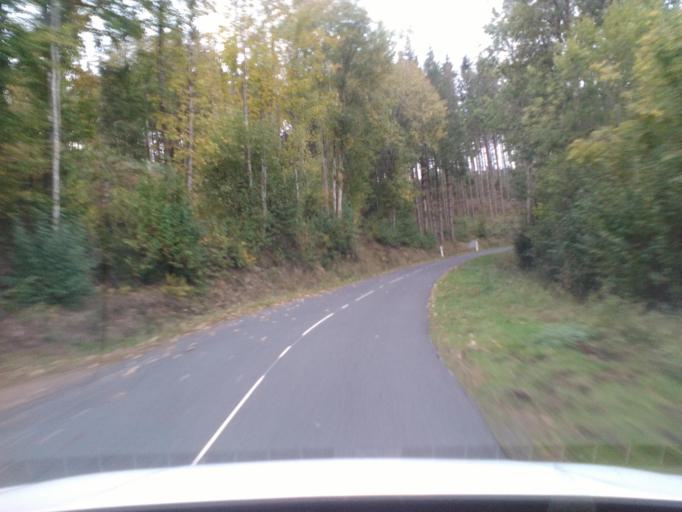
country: FR
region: Lorraine
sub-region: Departement des Vosges
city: Senones
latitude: 48.3767
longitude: 7.0425
